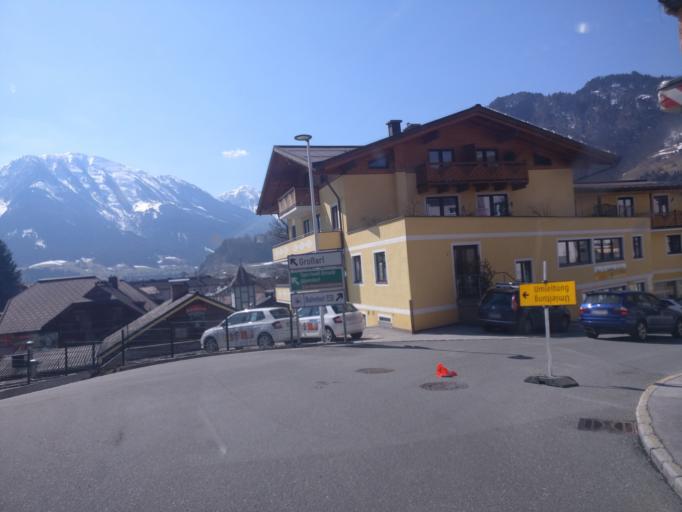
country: AT
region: Salzburg
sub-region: Politischer Bezirk Sankt Johann im Pongau
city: Sankt Johann im Pongau
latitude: 47.3453
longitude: 13.1999
